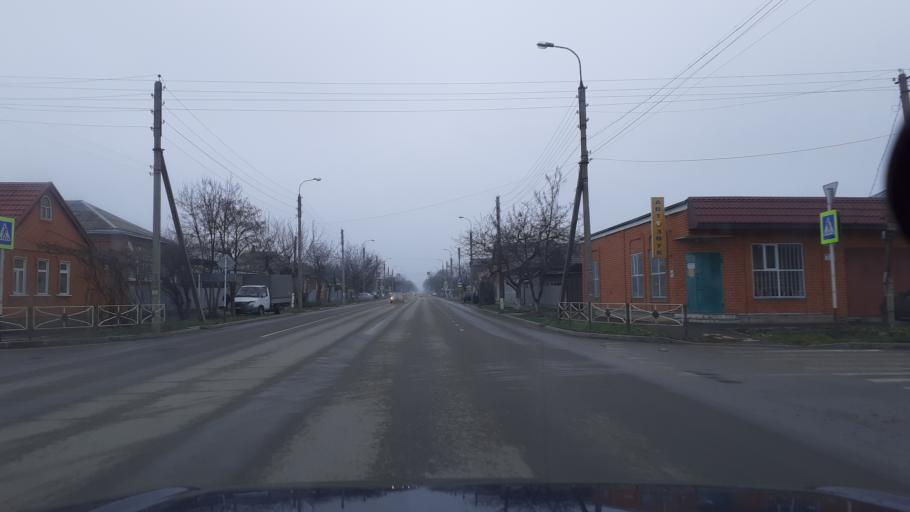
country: RU
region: Adygeya
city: Maykop
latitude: 44.6153
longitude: 40.0802
